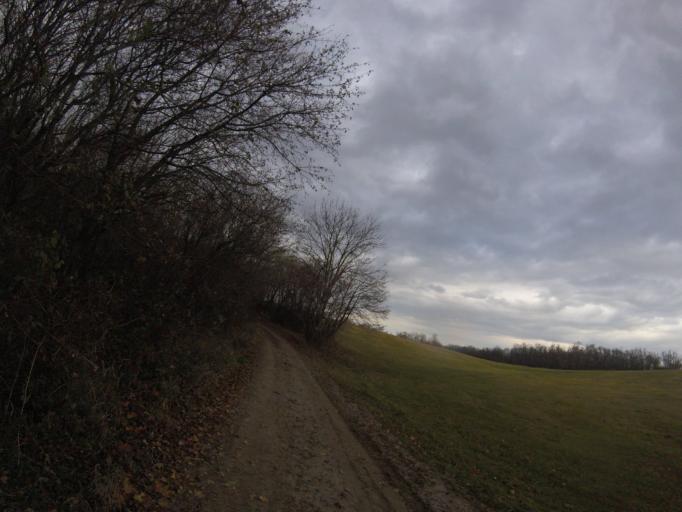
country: HU
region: Tolna
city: Szentgalpuszta
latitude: 46.3276
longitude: 18.6500
